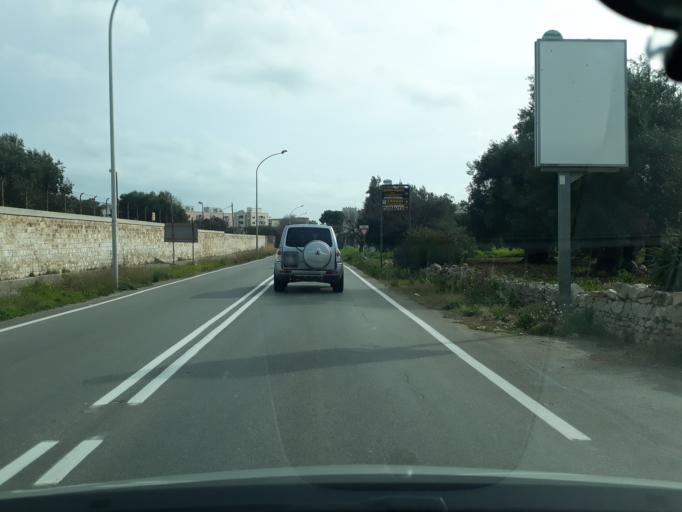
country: IT
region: Apulia
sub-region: Provincia di Bari
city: Monopoli
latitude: 40.9538
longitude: 17.2840
